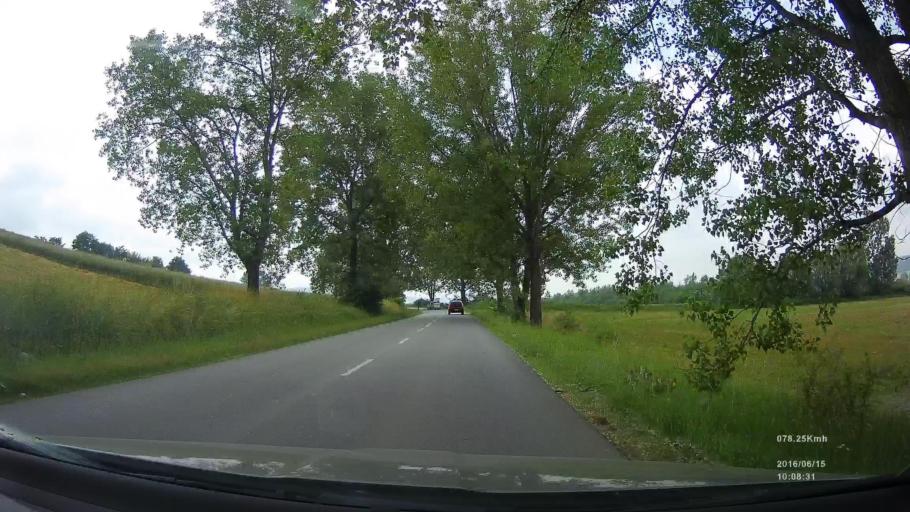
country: SK
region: Kosicky
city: Kosice
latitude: 48.7662
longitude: 21.3315
